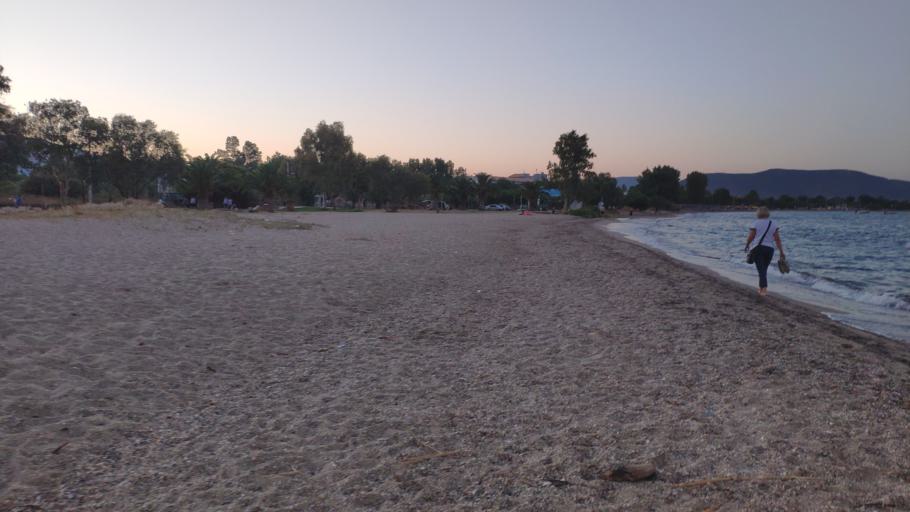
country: GR
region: Attica
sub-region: Nomarchia Anatolikis Attikis
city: Nea Makri
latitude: 38.1014
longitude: 23.9808
